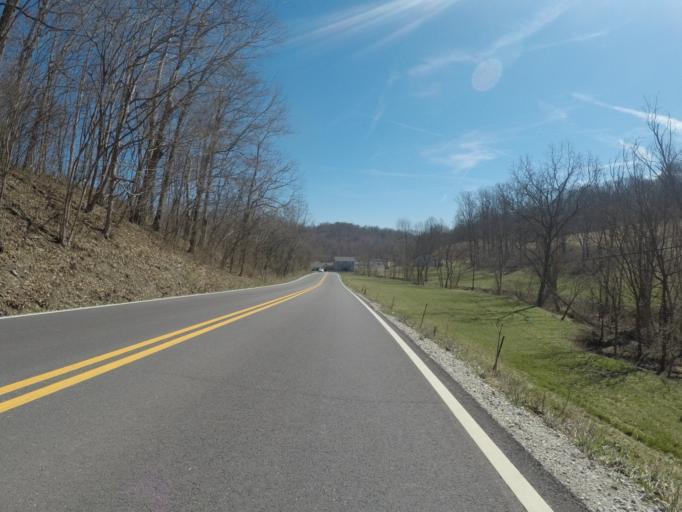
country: US
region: Ohio
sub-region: Lawrence County
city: Burlington
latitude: 38.4555
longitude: -82.5476
